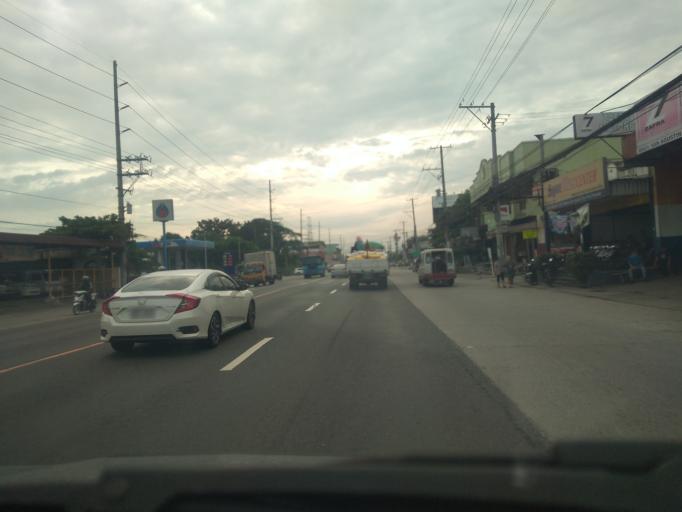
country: PH
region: Central Luzon
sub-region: Province of Pampanga
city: Magliman
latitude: 15.0474
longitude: 120.6687
